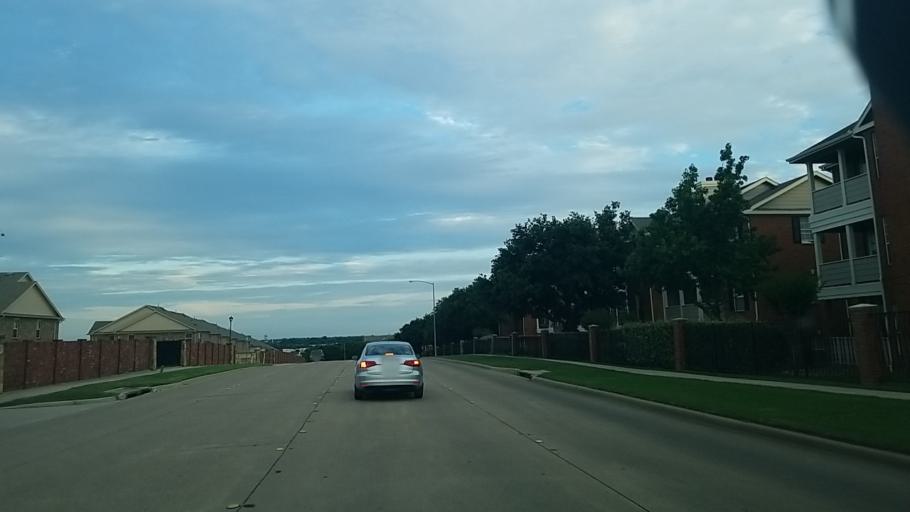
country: US
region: Texas
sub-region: Denton County
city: Lewisville
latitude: 33.0022
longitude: -96.9825
